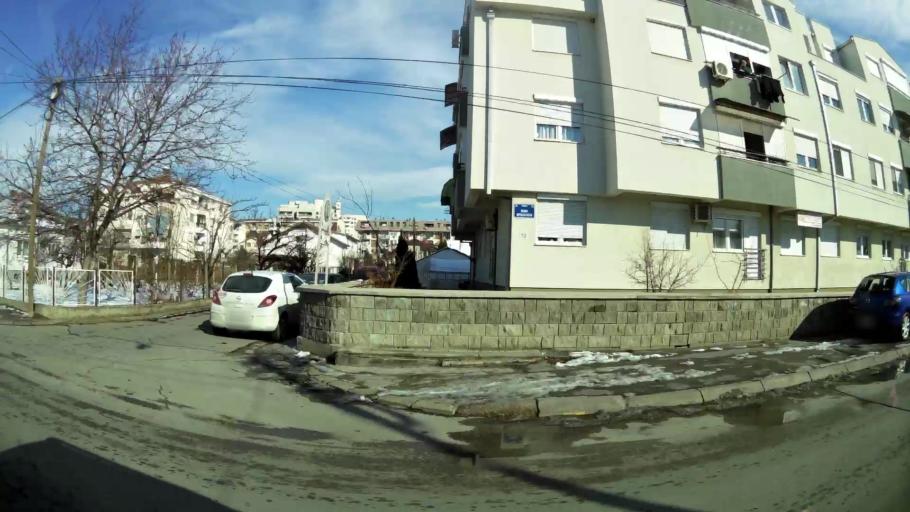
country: MK
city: Krushopek
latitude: 42.0051
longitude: 21.3675
